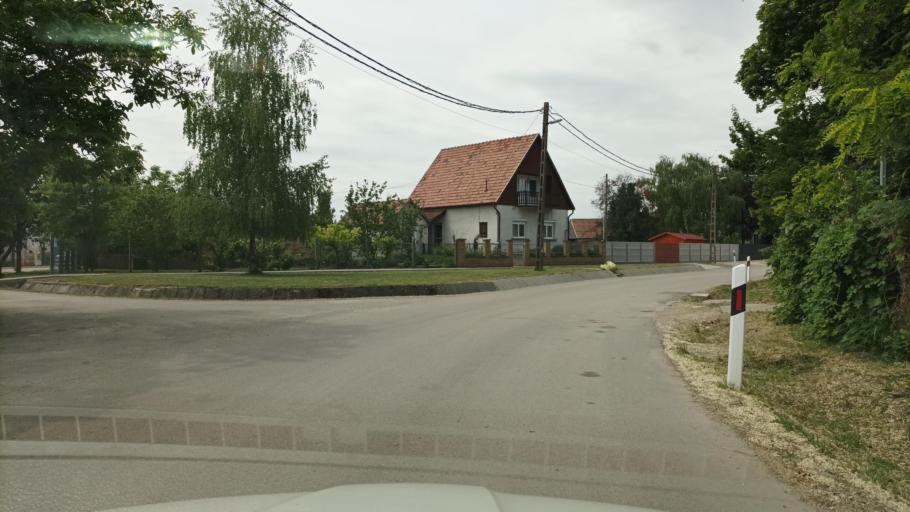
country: HU
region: Fejer
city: Adony
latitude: 47.1141
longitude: 18.8996
